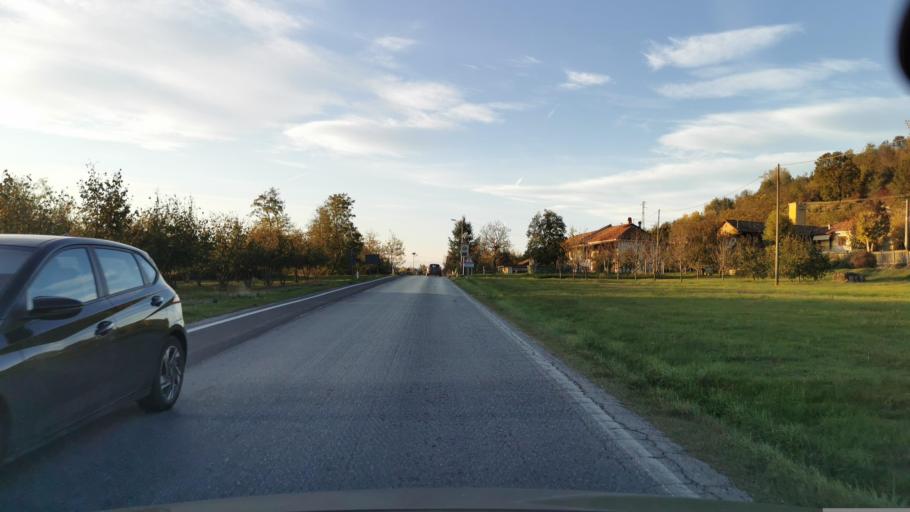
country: IT
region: Piedmont
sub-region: Provincia di Cuneo
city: Monchiero Borgonuovo
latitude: 44.5753
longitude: 7.9163
